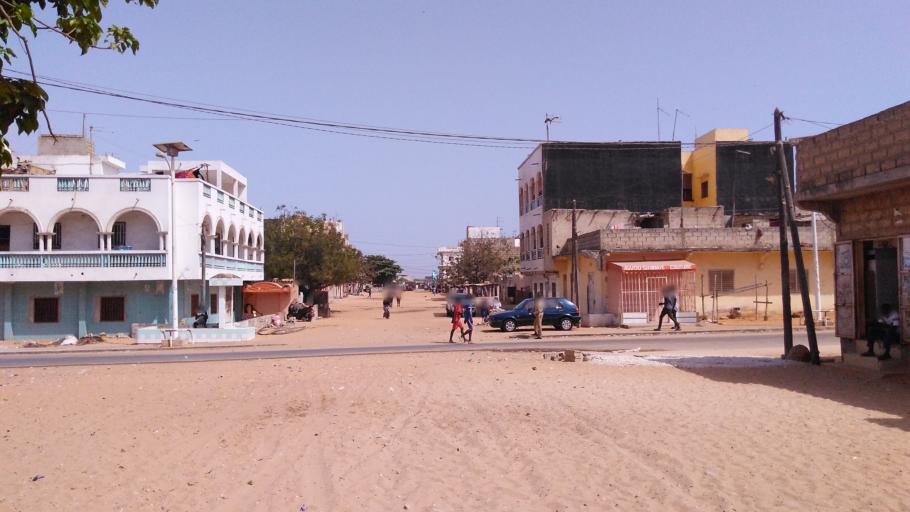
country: SN
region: Dakar
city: Pikine
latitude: 14.7785
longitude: -17.3780
